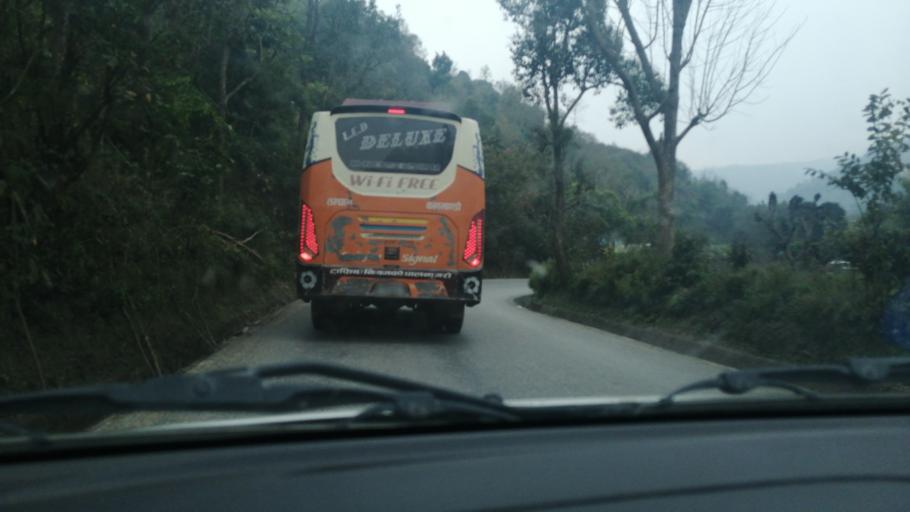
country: NP
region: Western Region
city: Tansen
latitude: 27.8144
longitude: 83.5311
